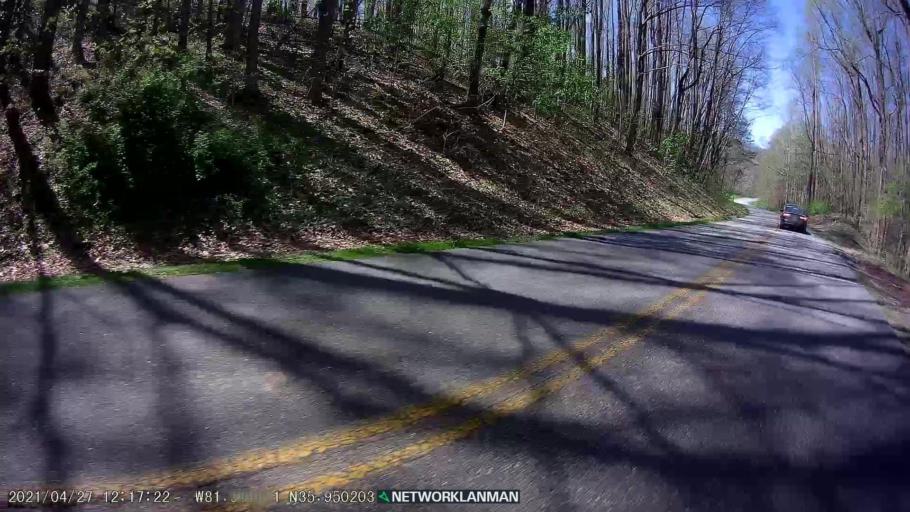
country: US
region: North Carolina
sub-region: Mitchell County
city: Spruce Pine
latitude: 35.9504
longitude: -81.9606
